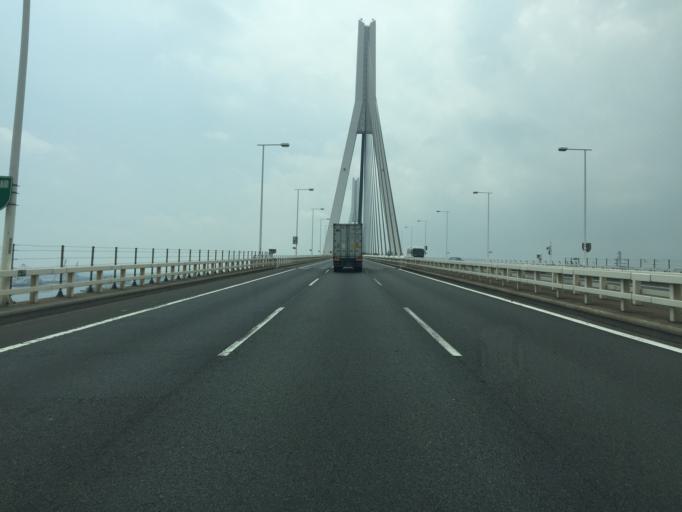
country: JP
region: Kanagawa
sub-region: Kawasaki-shi
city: Kawasaki
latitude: 35.4745
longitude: 139.7049
